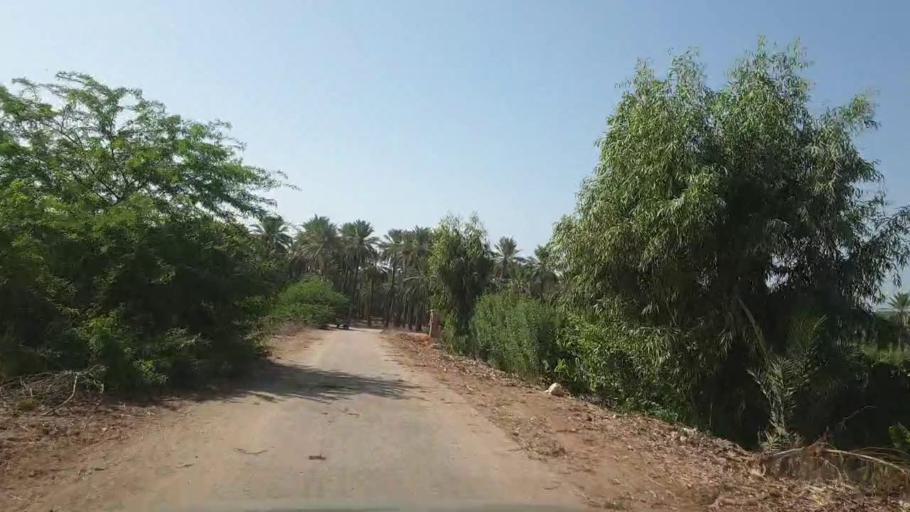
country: PK
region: Sindh
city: Rohri
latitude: 27.6310
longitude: 68.9076
